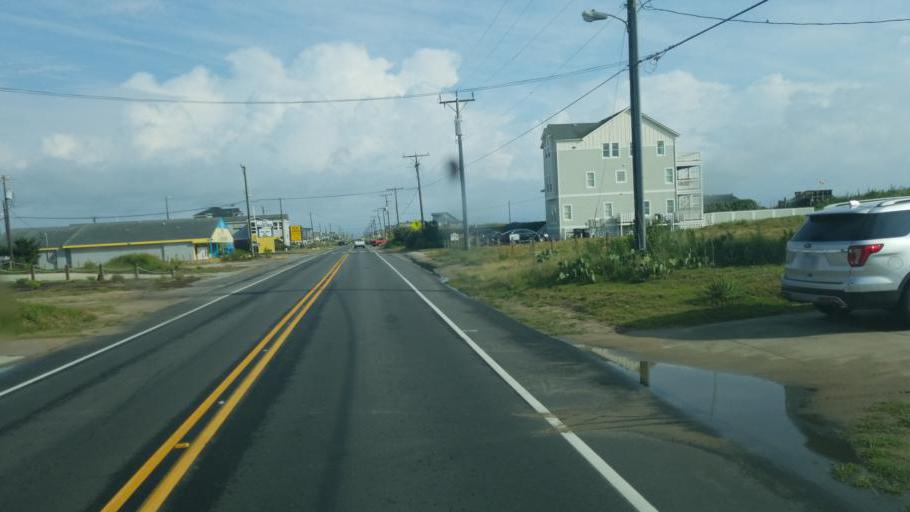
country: US
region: North Carolina
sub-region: Dare County
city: Kill Devil Hills
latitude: 36.0426
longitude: -75.6744
